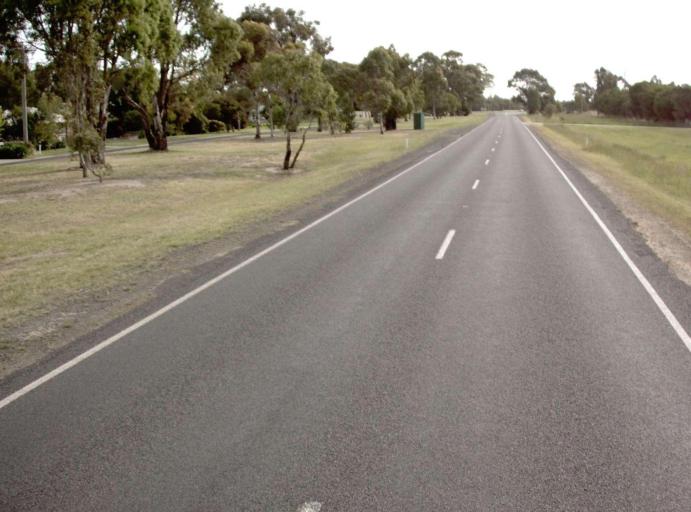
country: AU
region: Victoria
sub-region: Latrobe
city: Traralgon
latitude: -38.1258
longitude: 146.5676
